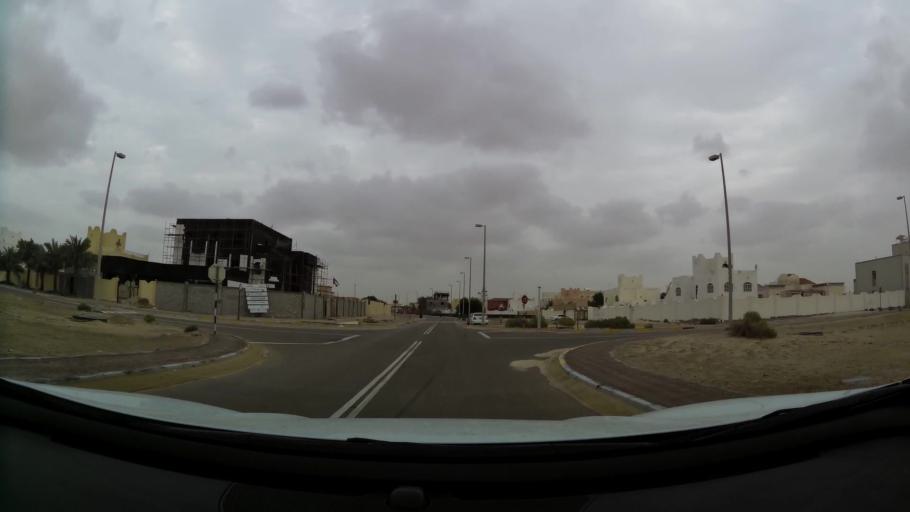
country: AE
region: Abu Dhabi
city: Abu Dhabi
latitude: 24.3808
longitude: 54.6535
